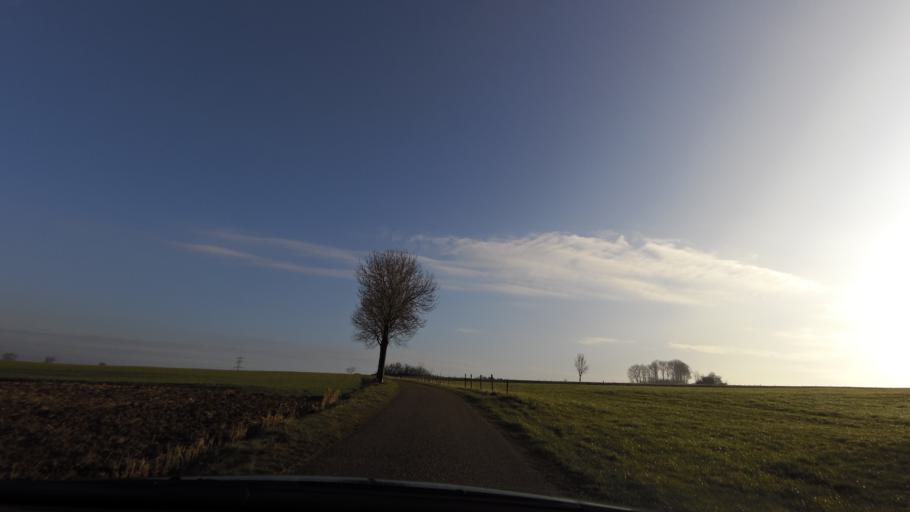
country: NL
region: Limburg
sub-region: Valkenburg aan de Geul
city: Schin op Geul
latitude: 50.8507
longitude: 5.8914
